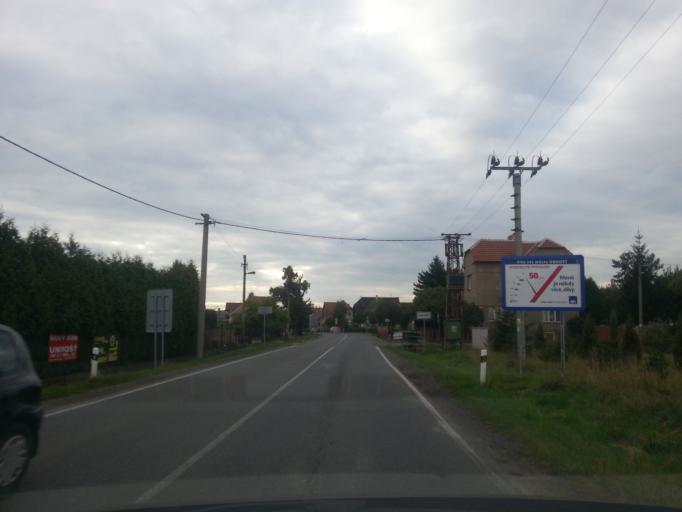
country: CZ
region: Central Bohemia
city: Unhost'
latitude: 50.0858
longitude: 14.1409
